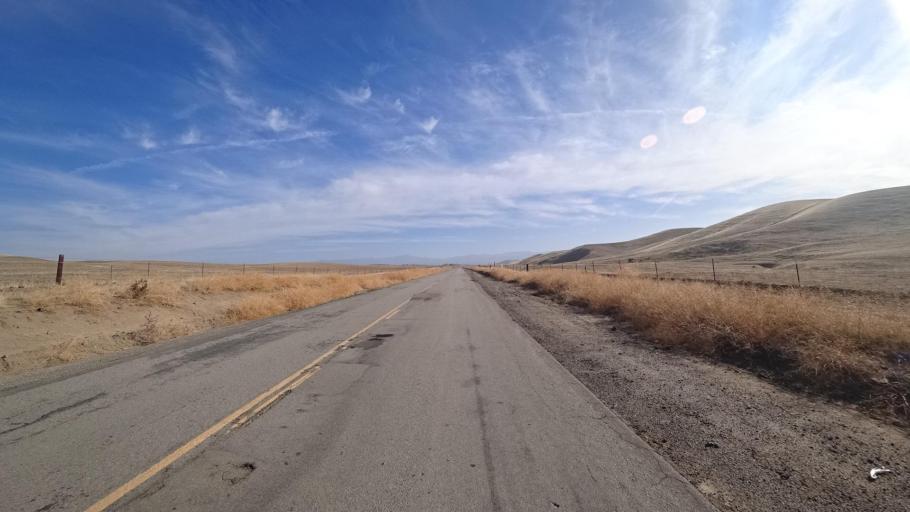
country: US
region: California
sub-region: Tulare County
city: Richgrove
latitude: 35.6229
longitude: -119.0072
